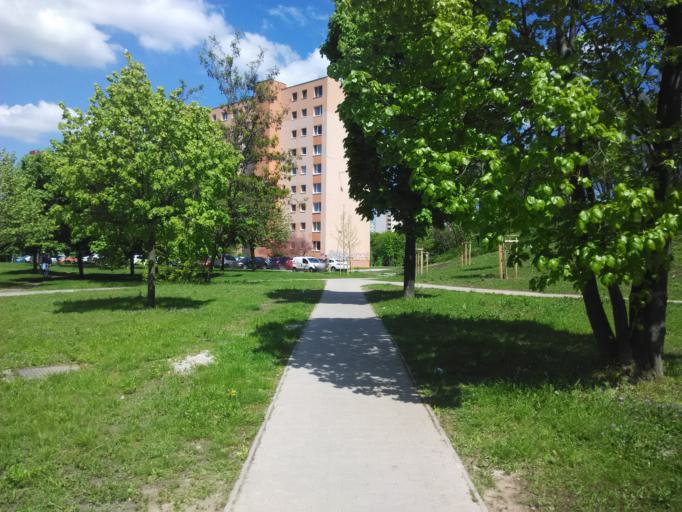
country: SK
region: Trnavsky
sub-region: Okres Trnava
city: Trnava
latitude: 48.3750
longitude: 17.5946
